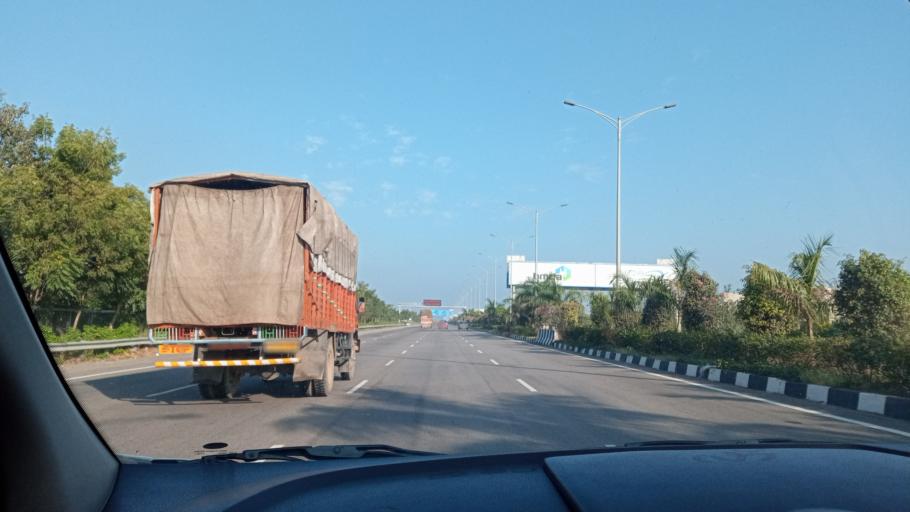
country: IN
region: Telangana
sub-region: Hyderabad
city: Hyderabad
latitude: 17.3327
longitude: 78.3700
